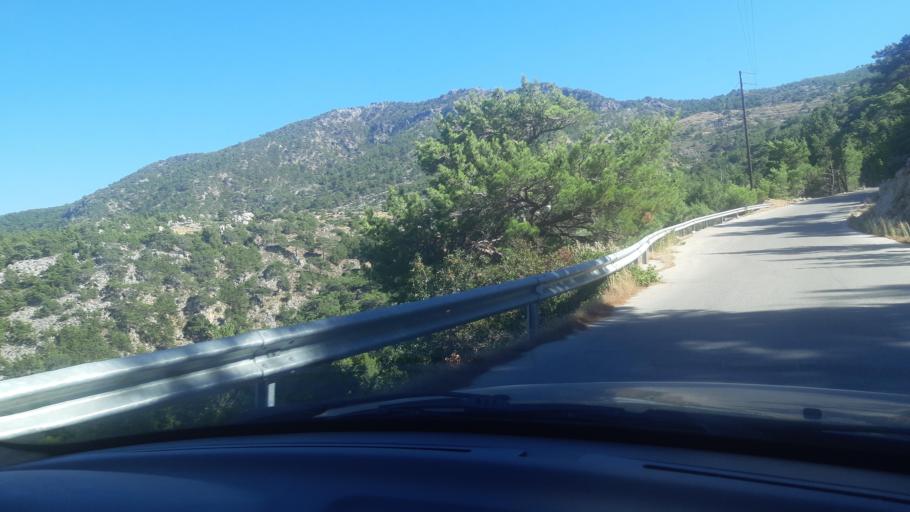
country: GR
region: South Aegean
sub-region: Nomos Dodekanisou
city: Karpathos
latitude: 35.5833
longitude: 27.1794
